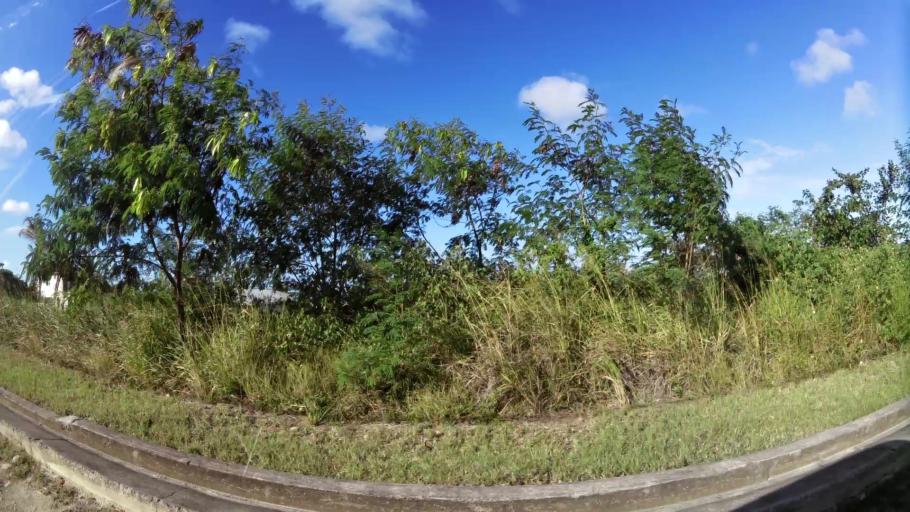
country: AG
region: Saint John
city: Potters Village
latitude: 17.0954
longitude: -61.8021
